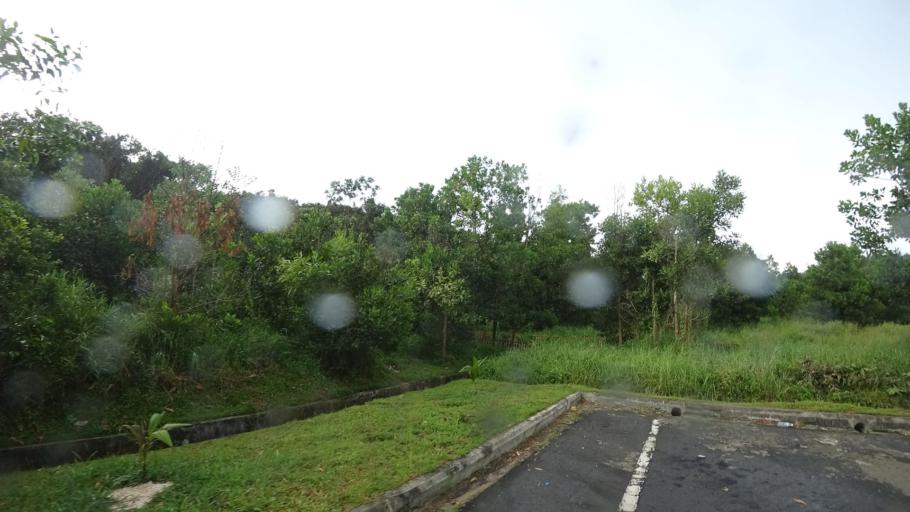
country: BN
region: Brunei and Muara
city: Bandar Seri Begawan
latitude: 4.8432
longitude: 114.9136
